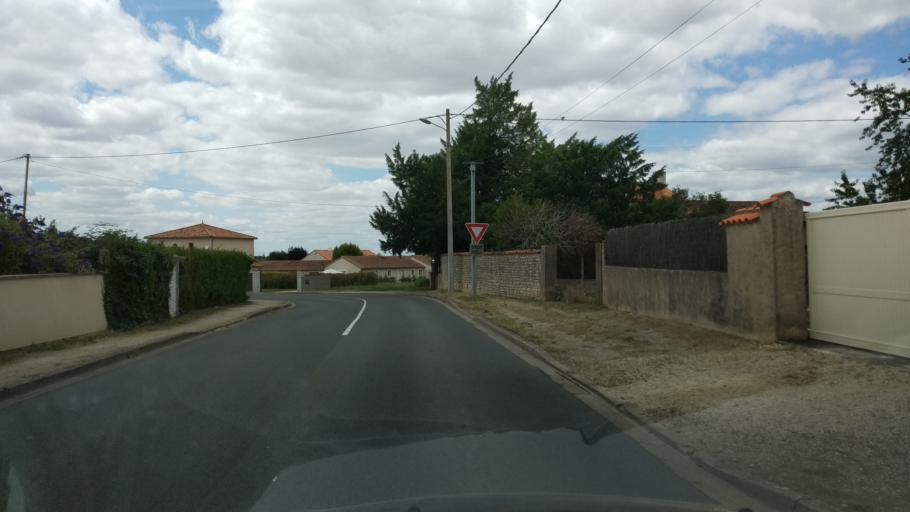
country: FR
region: Poitou-Charentes
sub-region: Departement de la Vienne
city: Avanton
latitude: 46.6640
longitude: 0.3068
